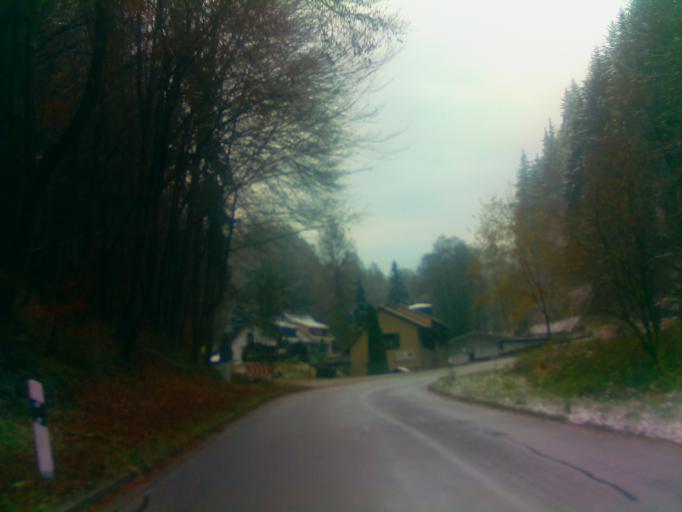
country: DE
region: Hesse
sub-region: Regierungsbezirk Darmstadt
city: Birkenau
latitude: 49.5258
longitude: 8.7338
